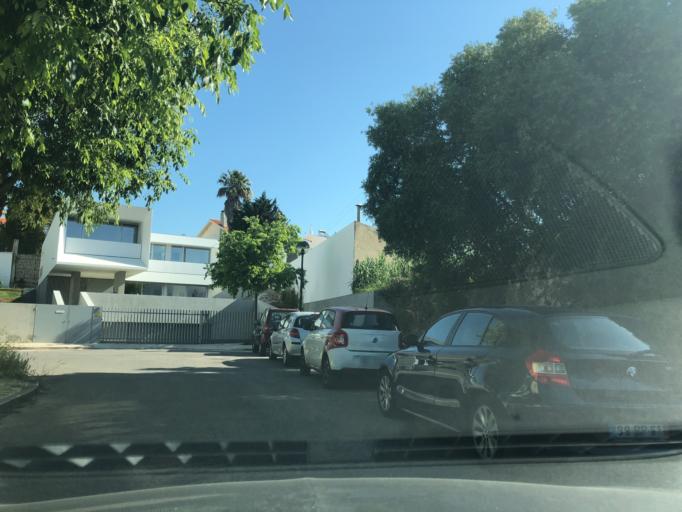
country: PT
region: Lisbon
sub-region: Oeiras
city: Paco de Arcos
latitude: 38.6964
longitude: -9.2983
